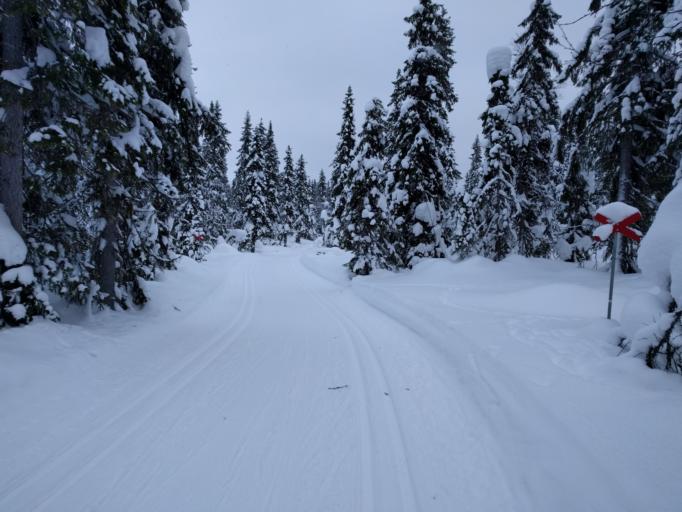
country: NO
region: Hedmark
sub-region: Trysil
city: Innbygda
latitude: 61.1510
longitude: 13.0375
